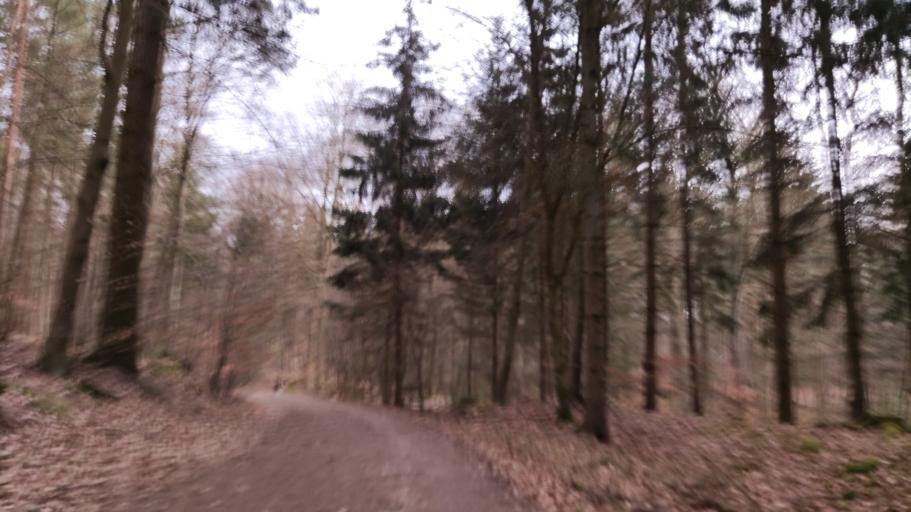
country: DE
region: Lower Saxony
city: Deutsch Evern
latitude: 53.2185
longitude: 10.4310
